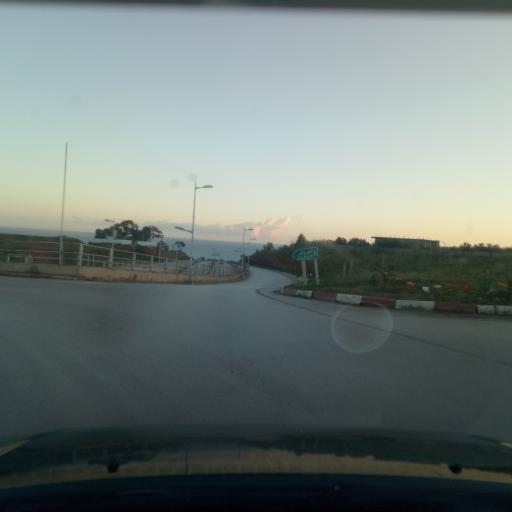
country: DZ
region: Tipaza
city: Bou Ismail
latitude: 36.6447
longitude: 2.7119
